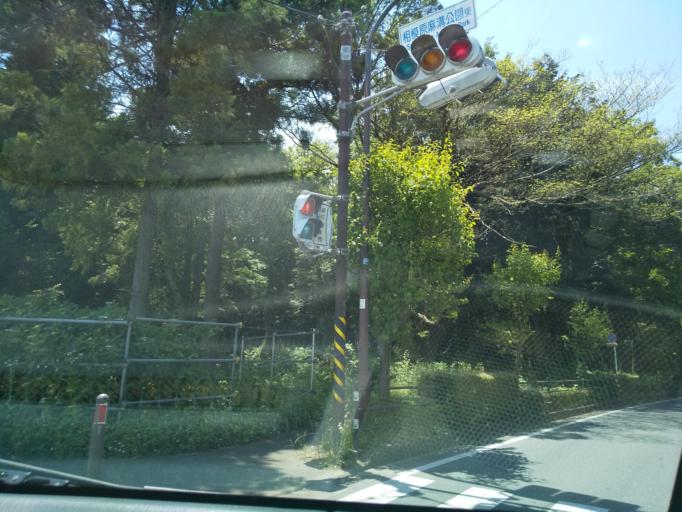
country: JP
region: Kanagawa
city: Zama
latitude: 35.5255
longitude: 139.3936
